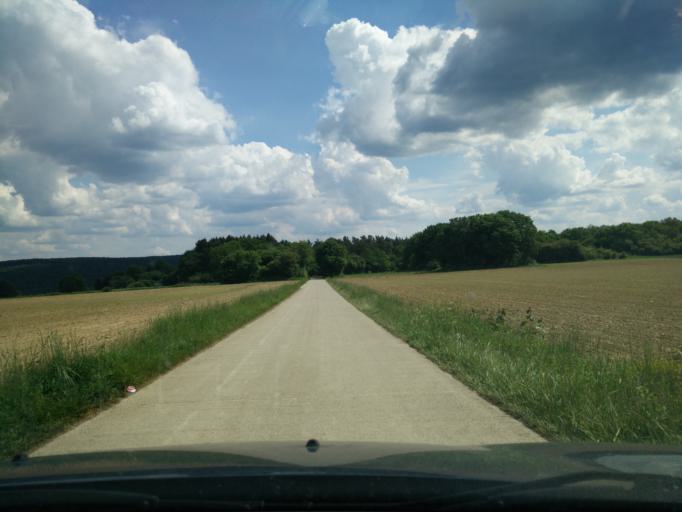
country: FR
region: Champagne-Ardenne
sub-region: Departement des Ardennes
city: Vireux-Molhain
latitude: 50.0862
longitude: 4.6184
